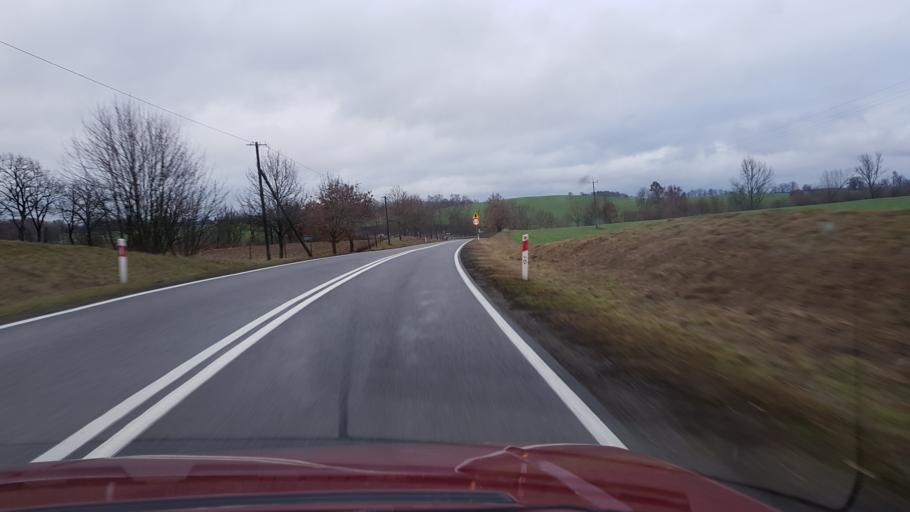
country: PL
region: West Pomeranian Voivodeship
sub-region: Powiat lobeski
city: Wegorzyno
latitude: 53.5095
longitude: 15.6471
